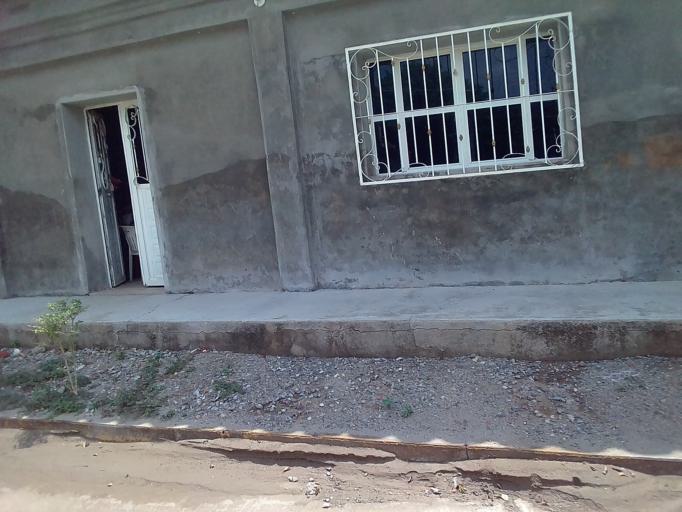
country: MX
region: Oaxaca
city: Union Hidalgo
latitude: 16.4677
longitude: -94.8267
